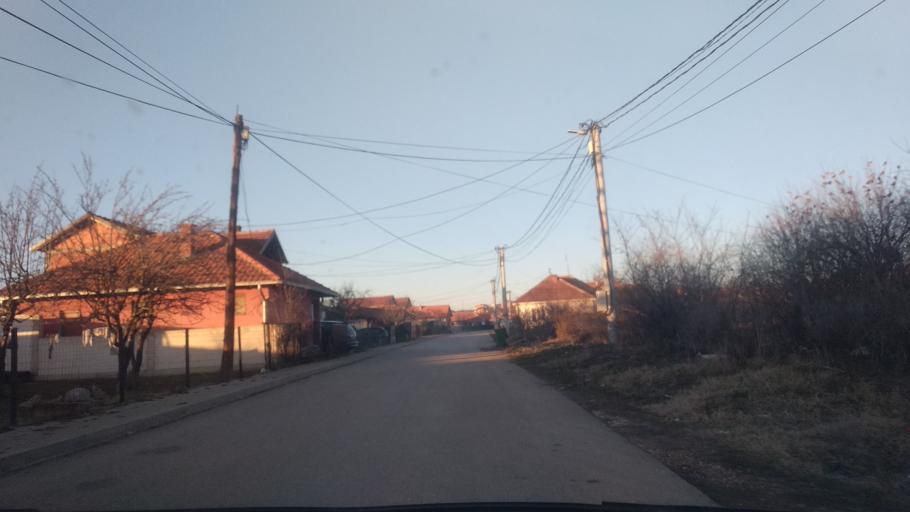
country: XK
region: Pristina
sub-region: Komuna e Prishtines
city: Pristina
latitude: 42.6032
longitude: 21.1826
